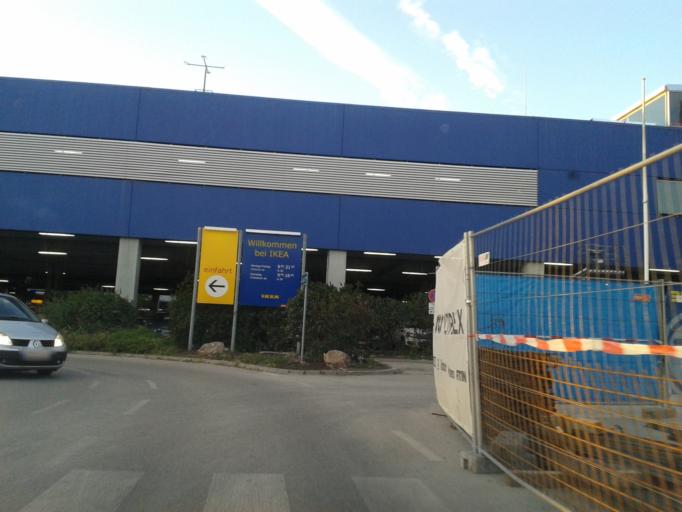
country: AT
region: Lower Austria
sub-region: Politischer Bezirk Modling
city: Wiener Neudorf
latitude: 48.1050
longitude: 16.3172
